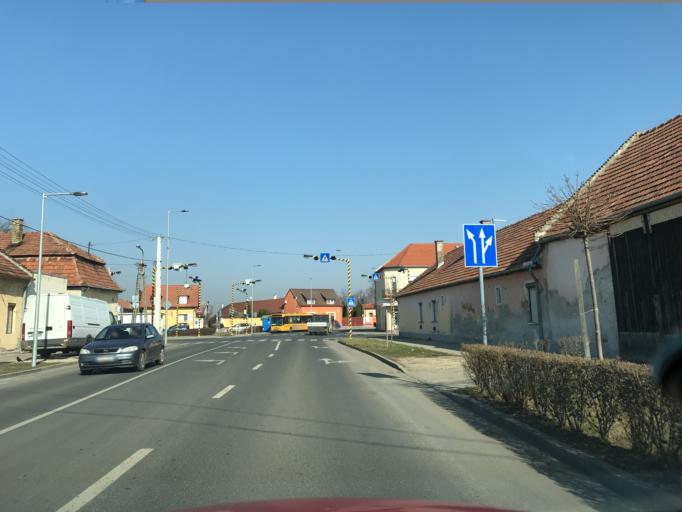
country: HU
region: Gyor-Moson-Sopron
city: Gyor
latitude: 47.6816
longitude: 17.6109
